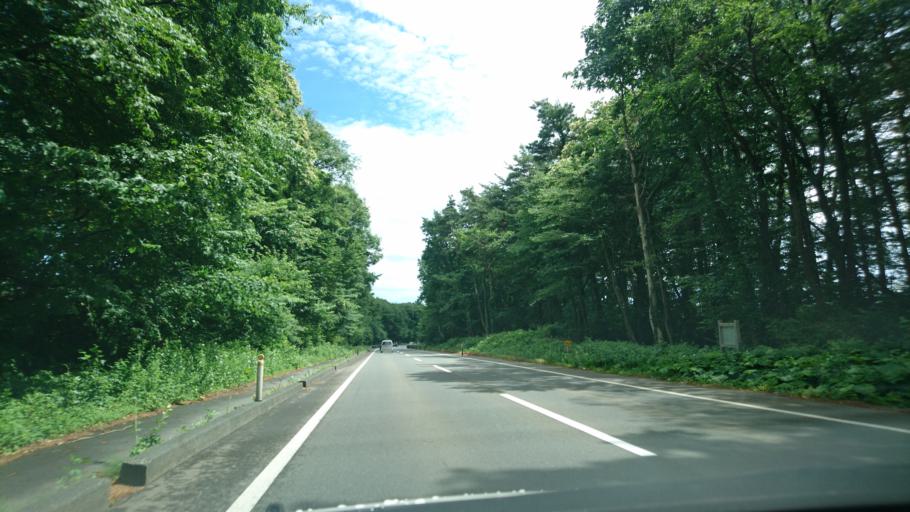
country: JP
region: Iwate
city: Morioka-shi
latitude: 39.7870
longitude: 141.1241
